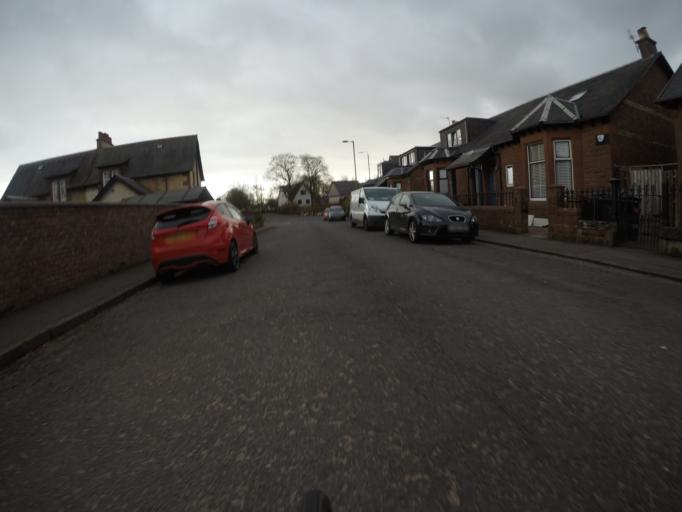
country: GB
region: Scotland
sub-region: East Ayrshire
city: Kilmarnock
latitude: 55.6156
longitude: -4.4872
